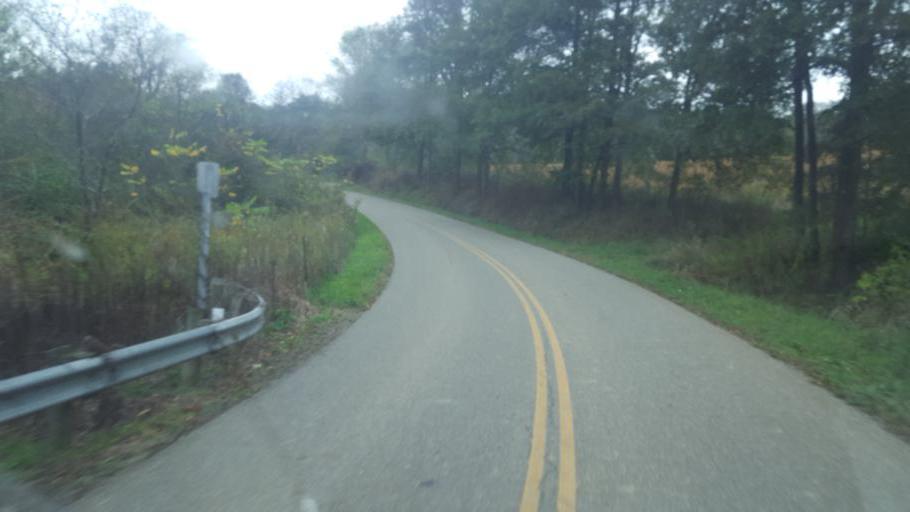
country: US
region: Ohio
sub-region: Carroll County
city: Carrollton
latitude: 40.4670
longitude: -81.0268
